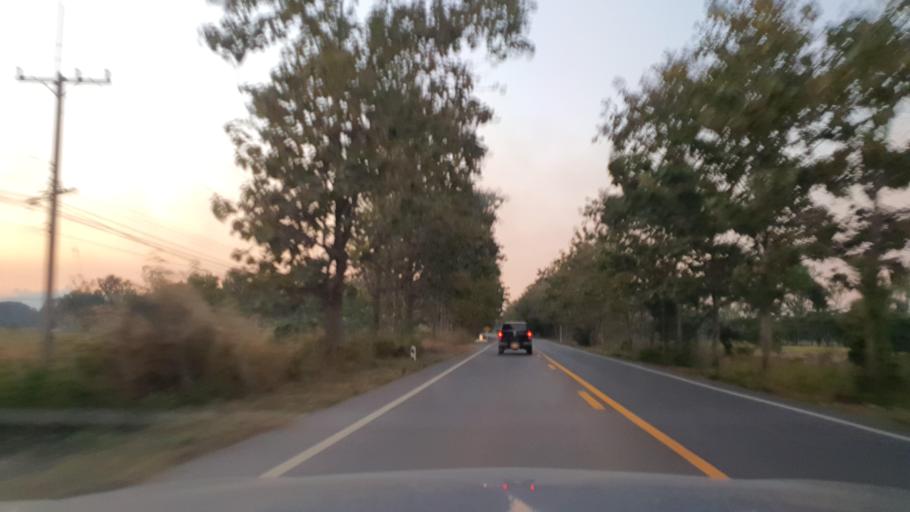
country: TH
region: Phayao
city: Dok Kham Tai
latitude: 19.1319
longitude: 100.0300
